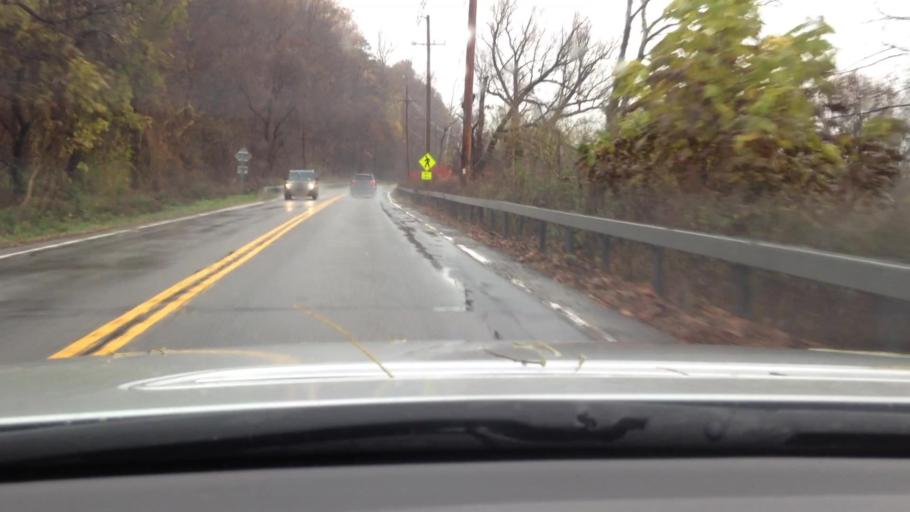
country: US
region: New York
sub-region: Putnam County
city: Cold Spring
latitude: 41.4387
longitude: -73.9729
